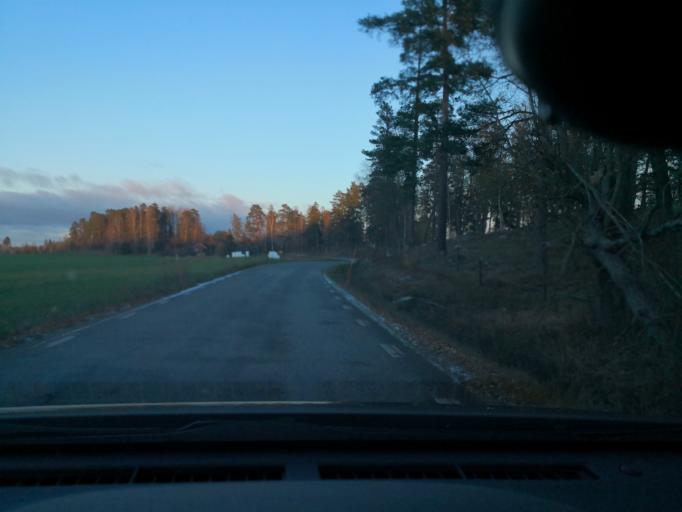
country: SE
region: Vaestmanland
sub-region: Vasteras
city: Tillberga
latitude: 59.7700
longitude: 16.5961
